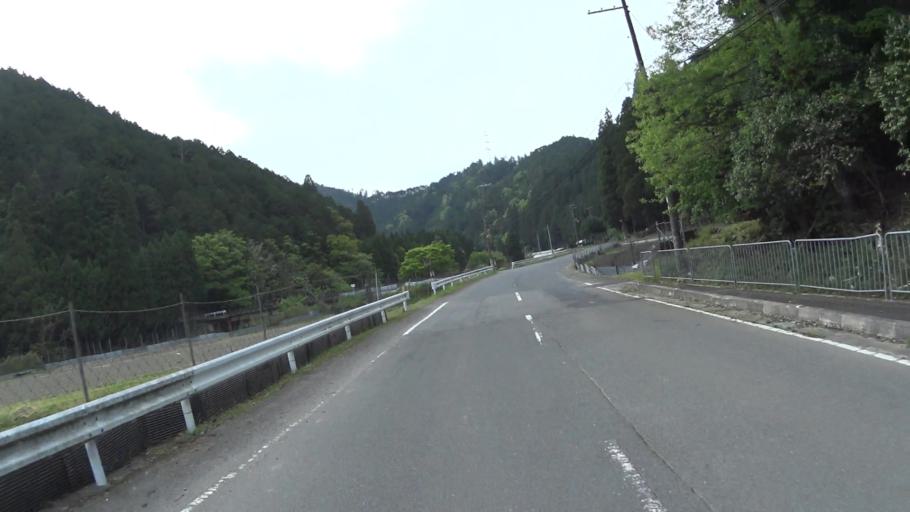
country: JP
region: Kyoto
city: Kameoka
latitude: 35.1201
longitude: 135.6083
